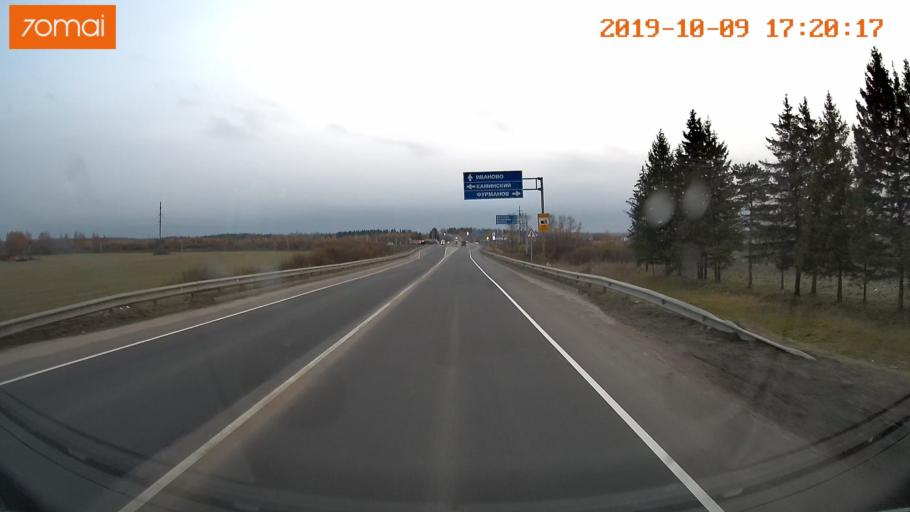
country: RU
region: Ivanovo
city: Furmanov
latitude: 57.2363
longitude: 41.1430
